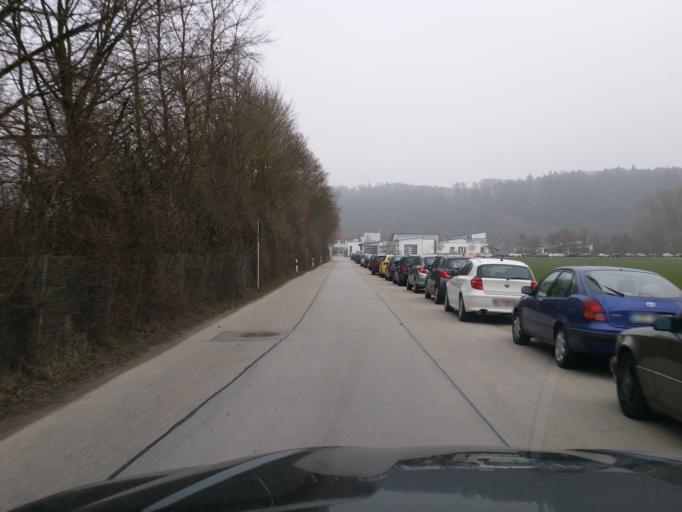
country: DE
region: Bavaria
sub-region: Lower Bavaria
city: Ergolding
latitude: 48.5576
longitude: 12.1928
